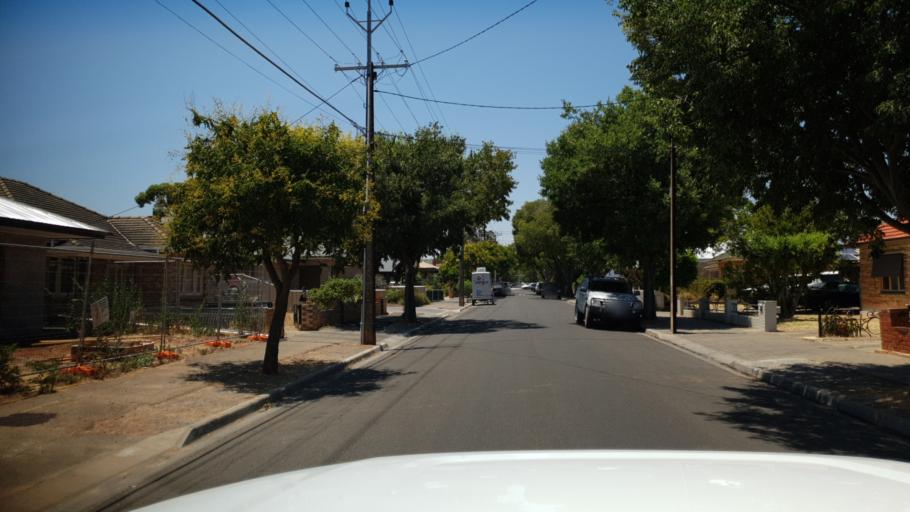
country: AU
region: South Australia
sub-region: Mitcham
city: Clarence Gardens
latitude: -34.9747
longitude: 138.5801
